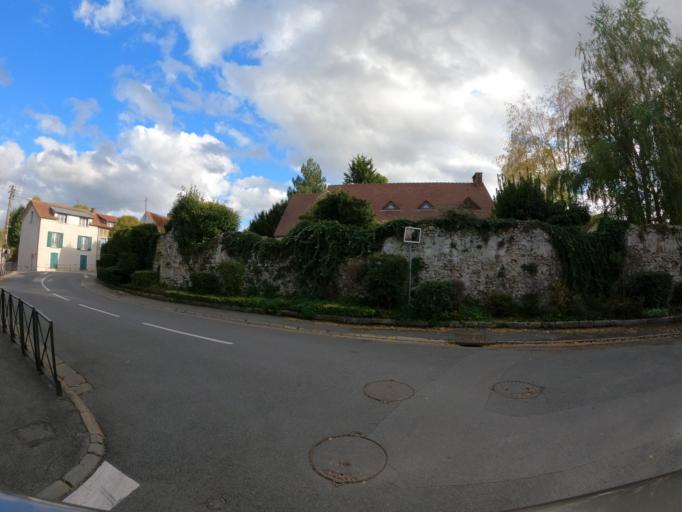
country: FR
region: Ile-de-France
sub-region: Departement de Seine-et-Marne
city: Chessy
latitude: 48.8799
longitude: 2.7618
